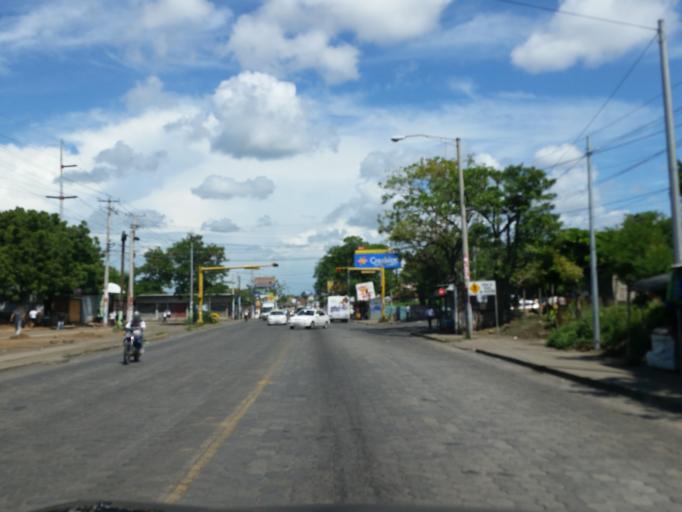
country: NI
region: Managua
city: Managua
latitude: 12.1290
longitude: -86.2227
